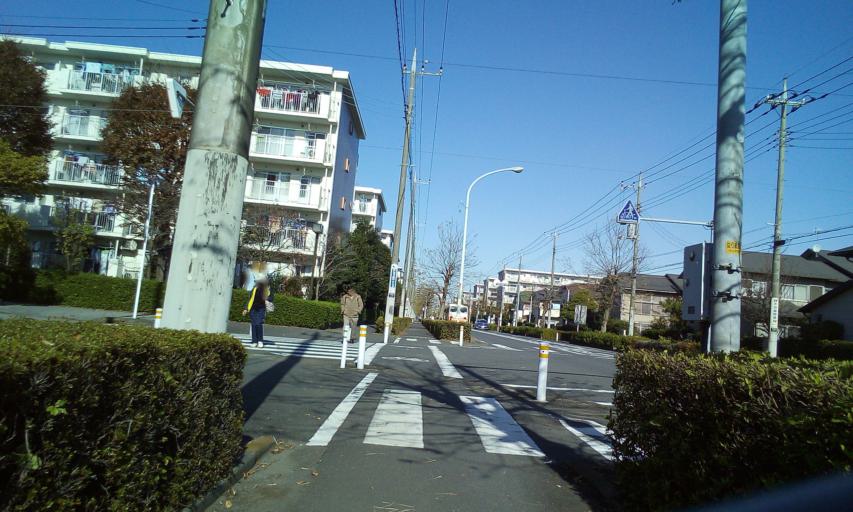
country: JP
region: Chiba
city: Nagareyama
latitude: 35.8512
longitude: 139.8853
